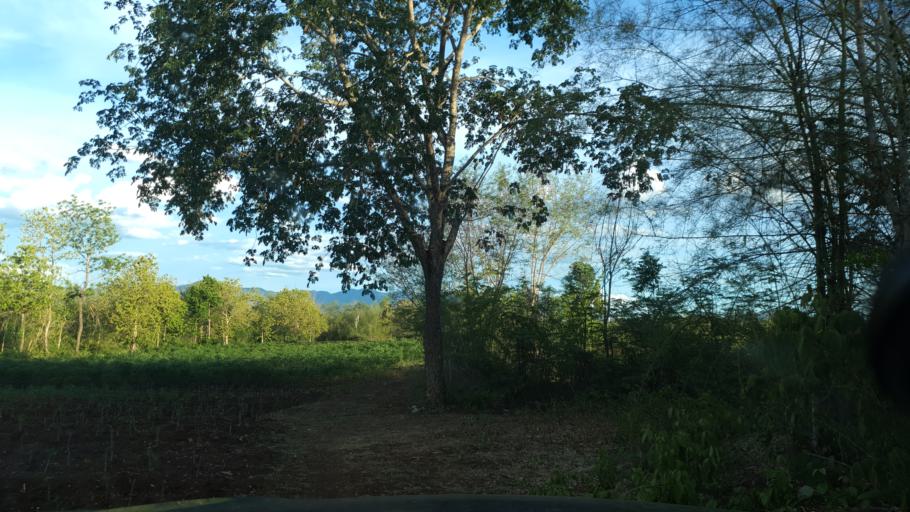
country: TH
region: Lampang
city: Sop Prap
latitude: 17.9628
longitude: 99.3519
